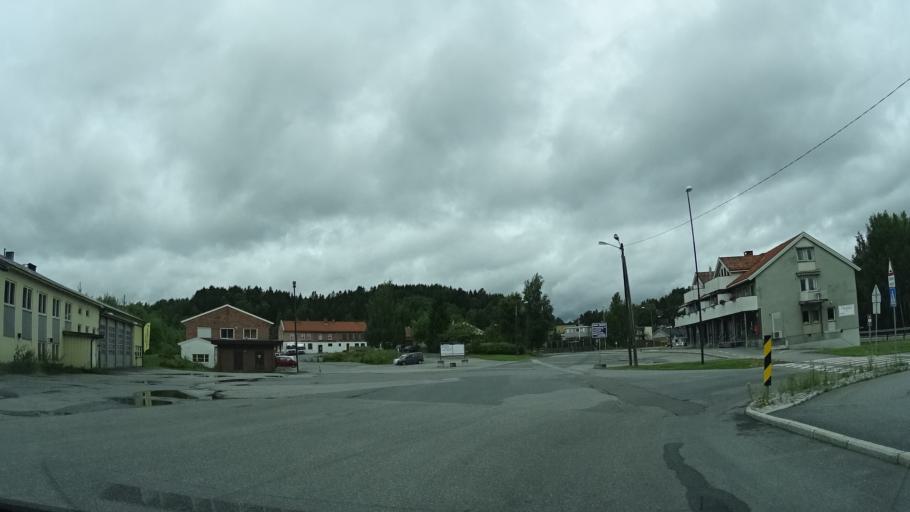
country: NO
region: Buskerud
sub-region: Ringerike
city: Honefoss
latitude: 60.1697
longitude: 10.2469
